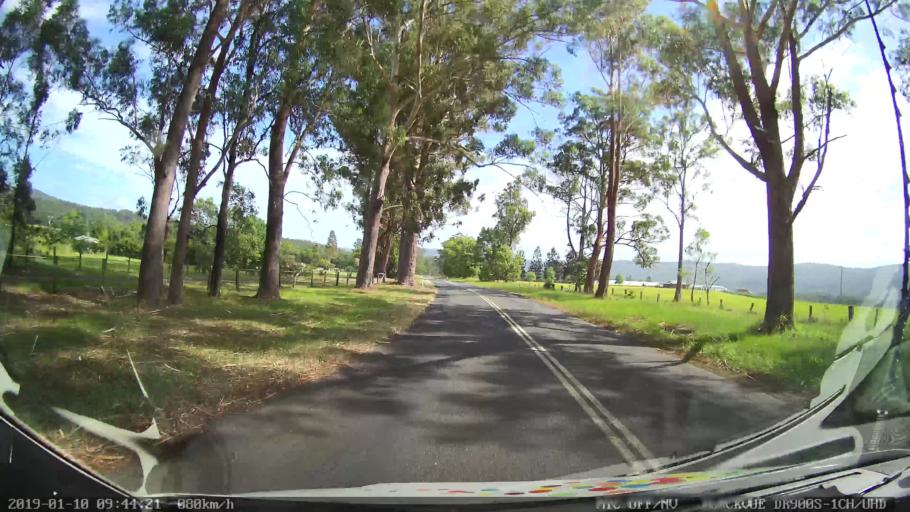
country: AU
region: New South Wales
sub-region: Coffs Harbour
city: Nana Glen
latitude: -30.1177
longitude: 153.0037
